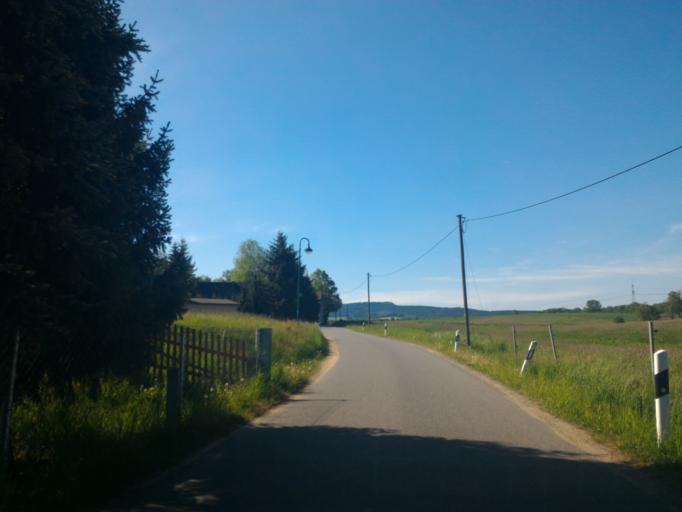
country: DE
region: Saxony
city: Niedercunnersdorf
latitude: 51.0519
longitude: 14.6573
